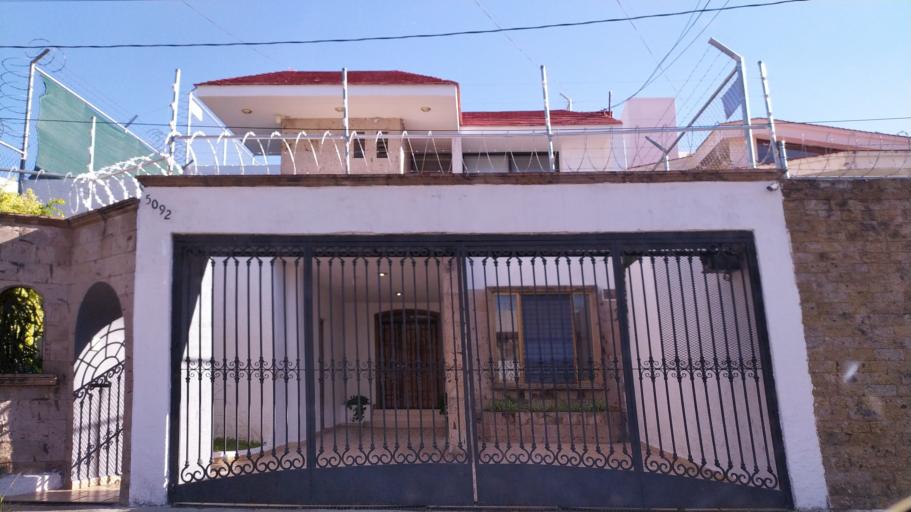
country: MX
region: Jalisco
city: Guadalajara
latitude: 20.6669
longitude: -103.4261
